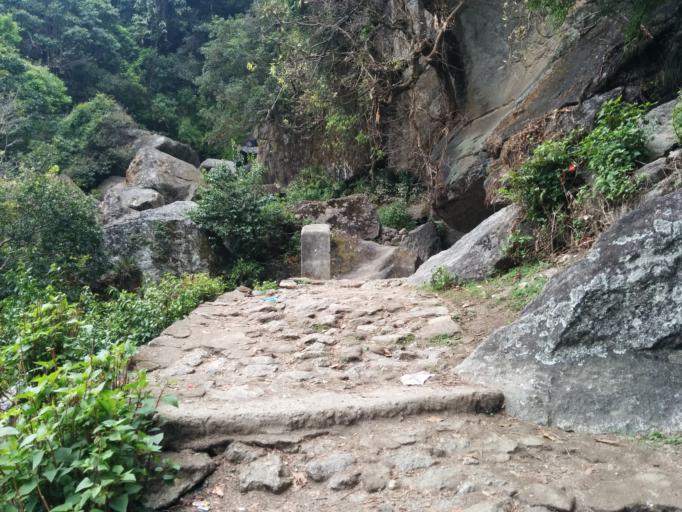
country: NP
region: Central Region
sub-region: Bagmati Zone
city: Bhaktapur
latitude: 27.7677
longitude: 85.4236
